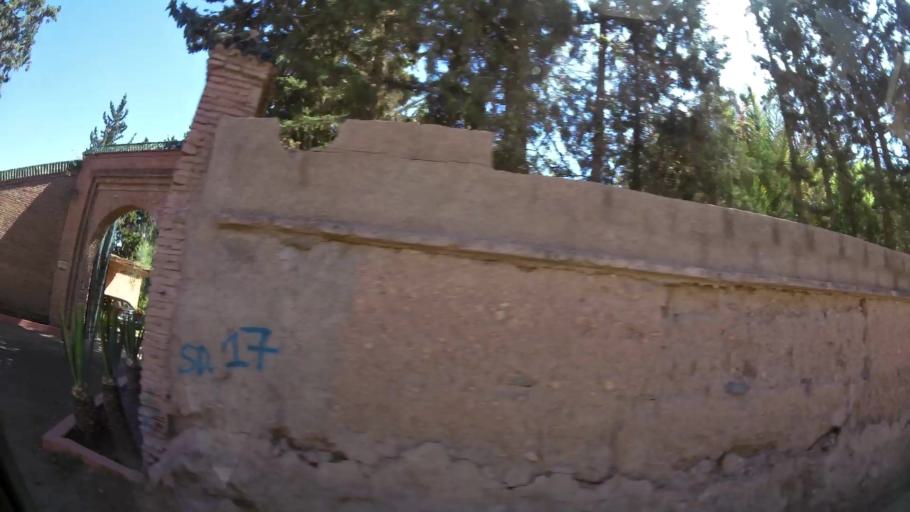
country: MA
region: Marrakech-Tensift-Al Haouz
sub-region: Marrakech
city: Marrakesh
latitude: 31.6684
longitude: -7.9596
